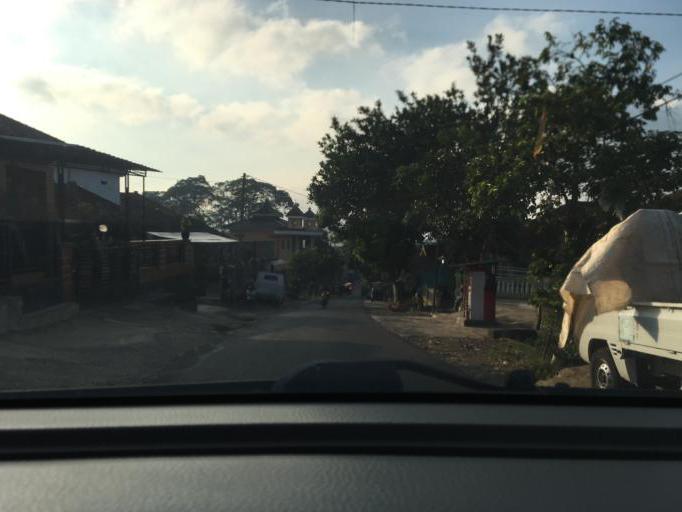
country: ID
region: West Java
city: Nagarakembang
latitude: -7.0368
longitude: 108.3291
